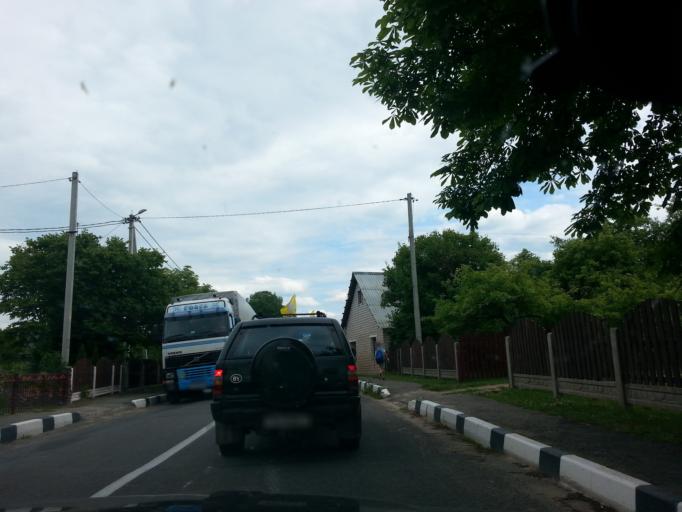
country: BY
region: Minsk
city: Narach
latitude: 54.8916
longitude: 26.7711
